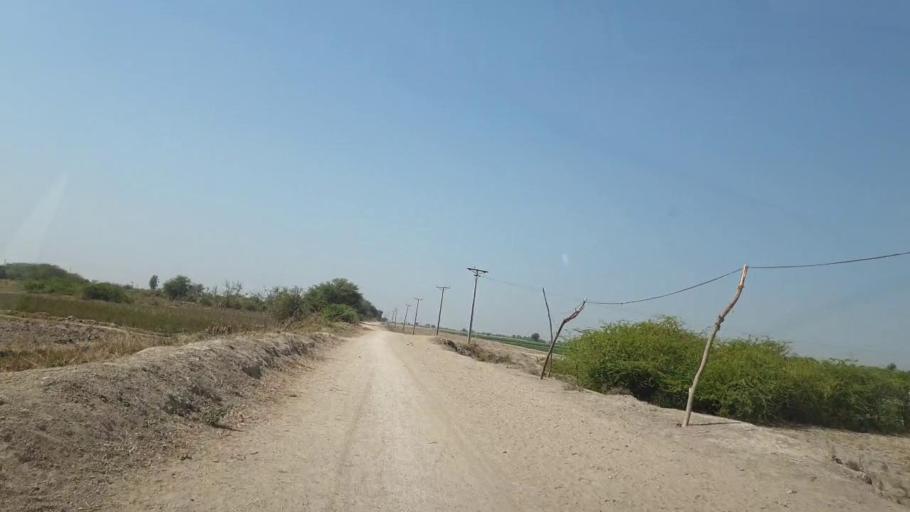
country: PK
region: Sindh
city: Kunri
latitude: 25.0995
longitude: 69.4581
